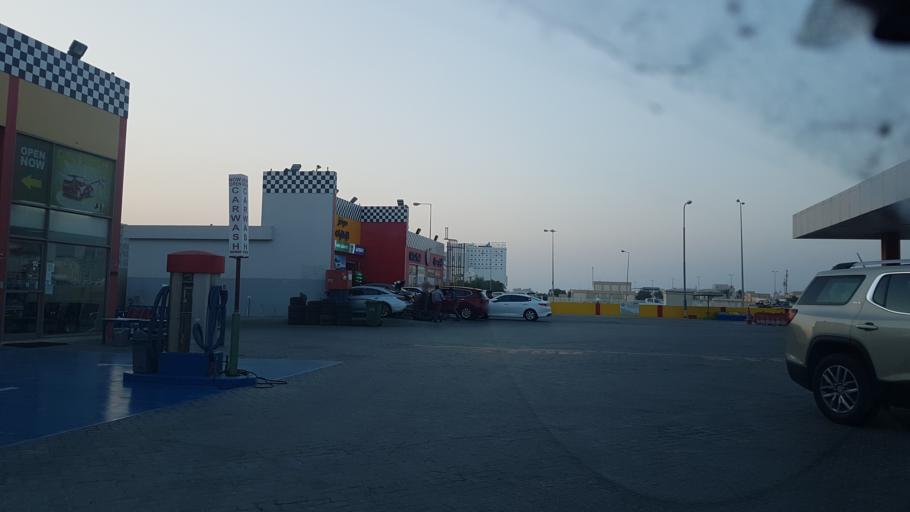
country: BH
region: Northern
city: Ar Rifa'
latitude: 26.1499
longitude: 50.5735
